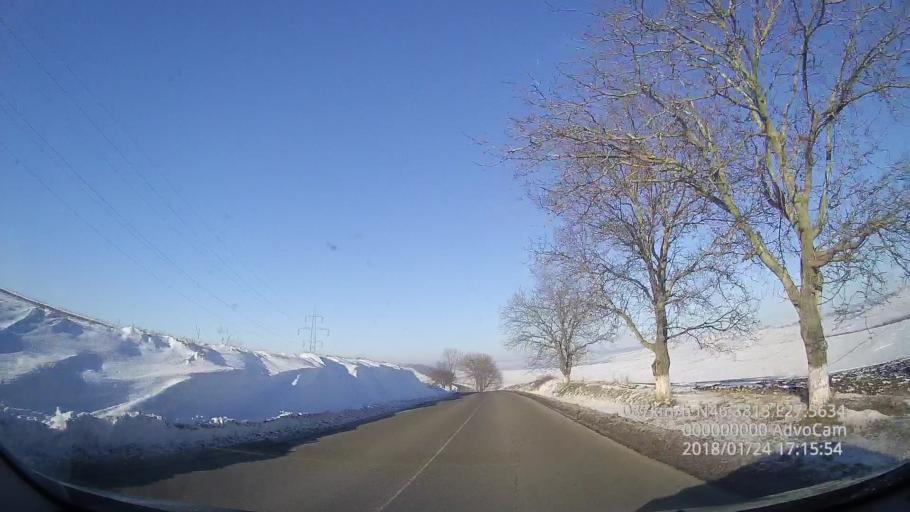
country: RO
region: Vaslui
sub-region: Comuna Rebricea
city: Rebricea
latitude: 46.8820
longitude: 27.5636
